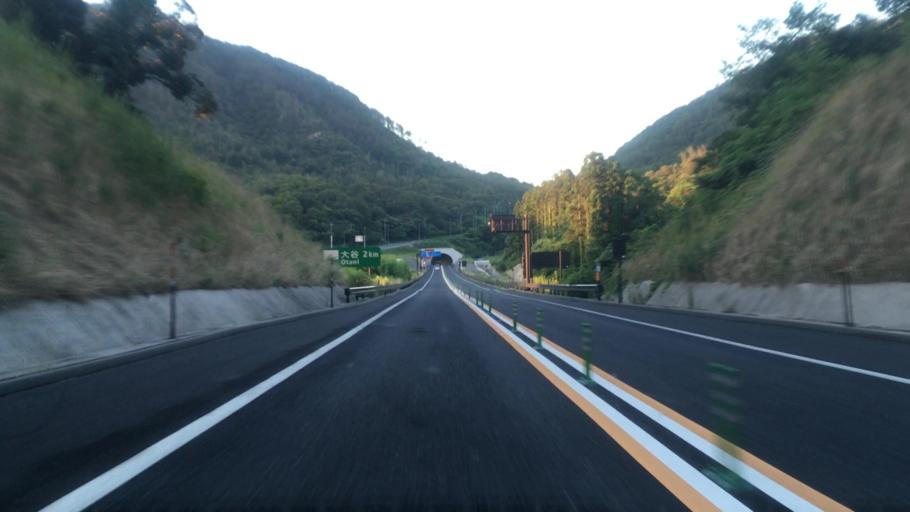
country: JP
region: Tottori
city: Tottori
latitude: 35.5573
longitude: 134.2825
